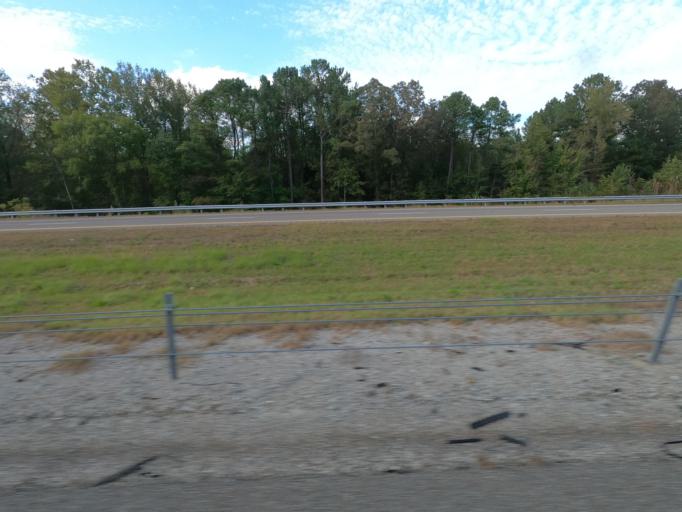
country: US
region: Tennessee
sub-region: Henderson County
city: Lexington
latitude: 35.8111
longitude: -88.2977
